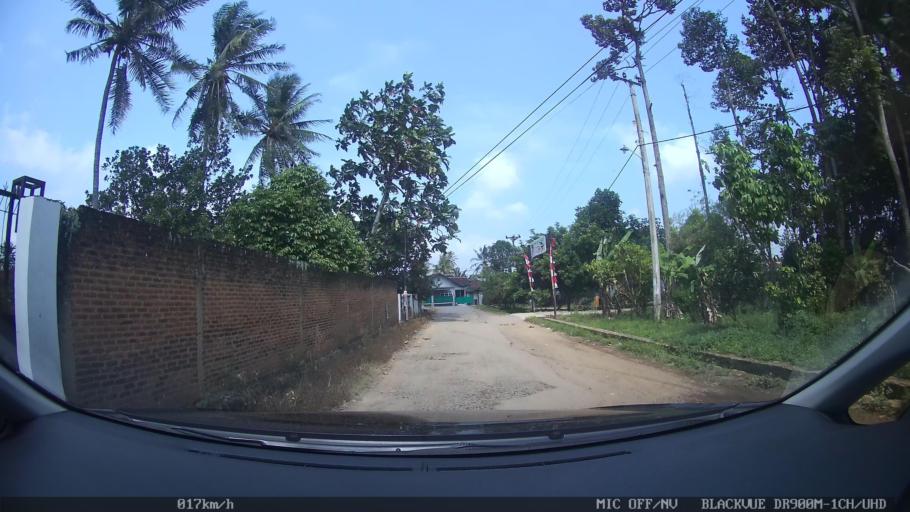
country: ID
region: Lampung
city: Kedaton
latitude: -5.3460
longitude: 105.2890
